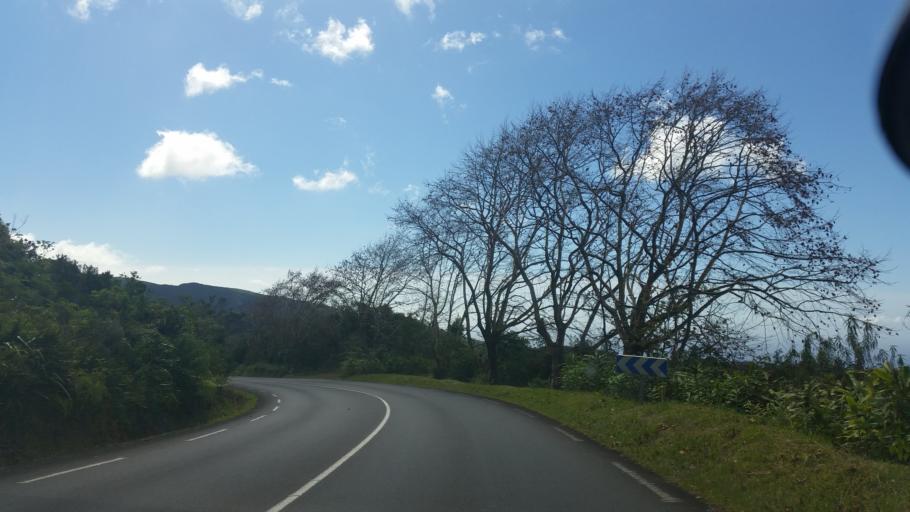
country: RE
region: Reunion
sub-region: Reunion
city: Saint-Benoit
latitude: -21.1141
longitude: 55.6566
